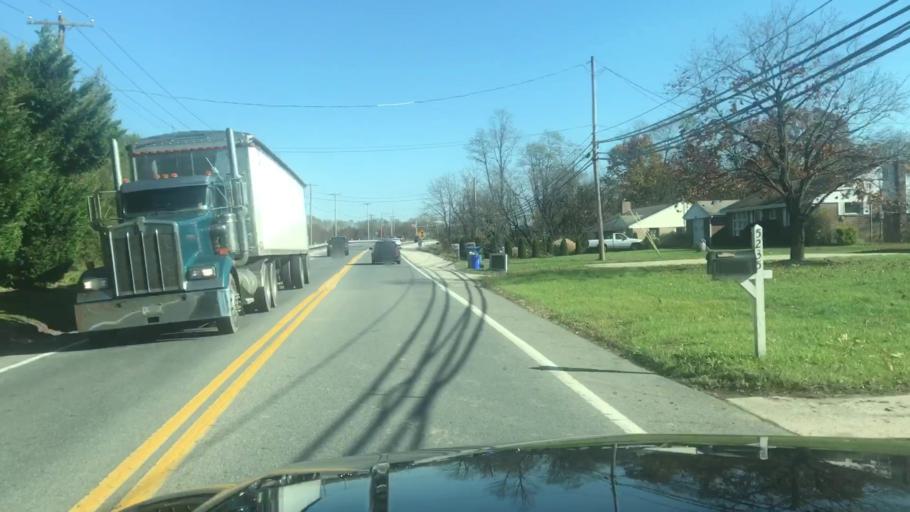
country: US
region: Pennsylvania
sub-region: Cumberland County
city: Enola
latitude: 40.2890
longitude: -76.9910
